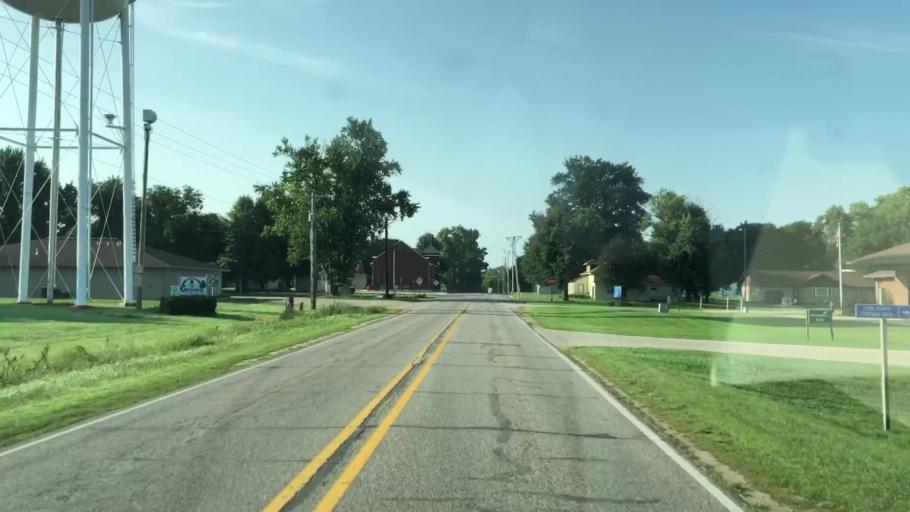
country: US
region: Iowa
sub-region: Lyon County
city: George
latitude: 43.3468
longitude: -95.9984
